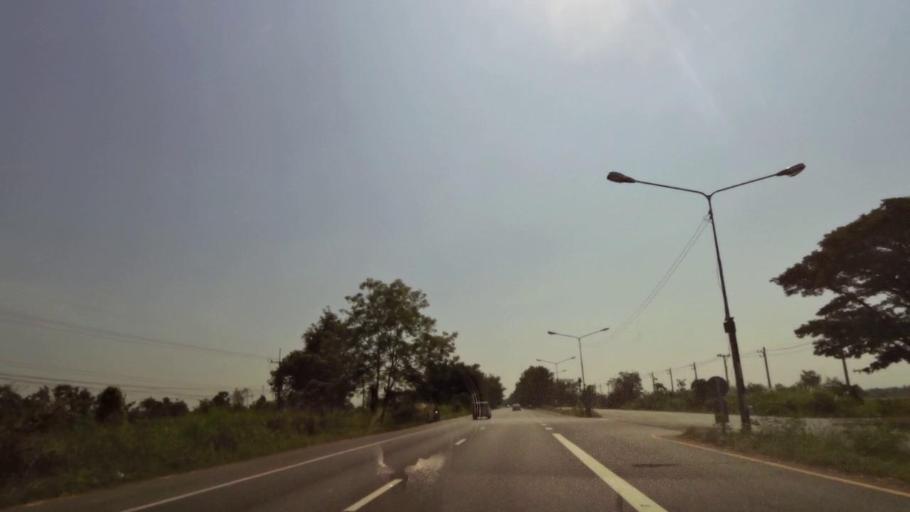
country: TH
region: Nakhon Sawan
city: Kao Liao
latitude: 15.9300
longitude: 100.1124
